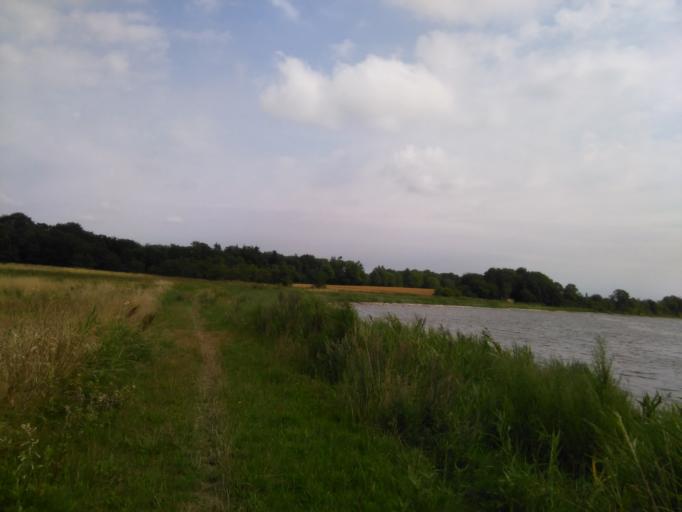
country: DK
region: Central Jutland
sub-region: Odder Kommune
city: Odder
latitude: 55.8783
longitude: 10.0447
